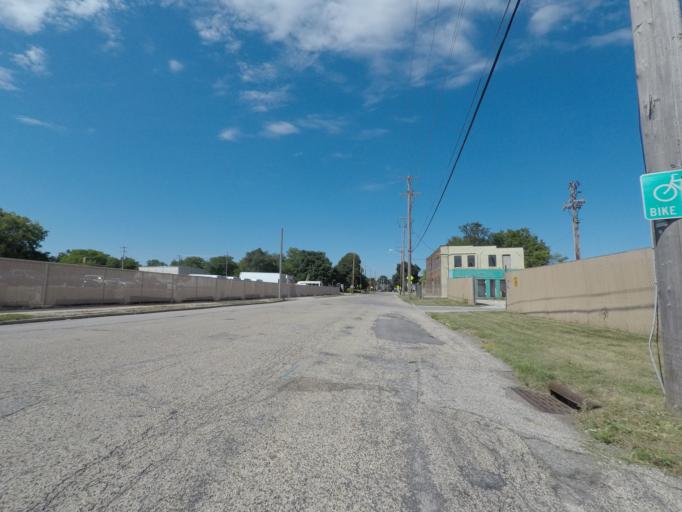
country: US
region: Wisconsin
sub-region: Waukesha County
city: Waukesha
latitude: 43.0095
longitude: -88.2112
